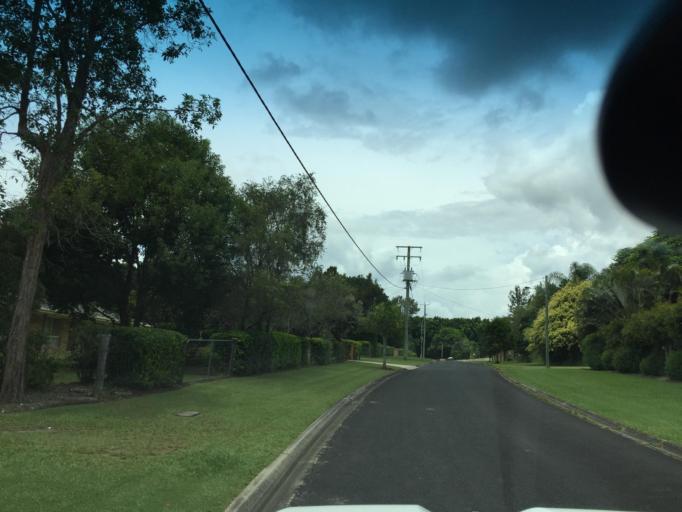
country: AU
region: Queensland
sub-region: Moreton Bay
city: Caboolture
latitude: -27.0409
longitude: 152.9231
